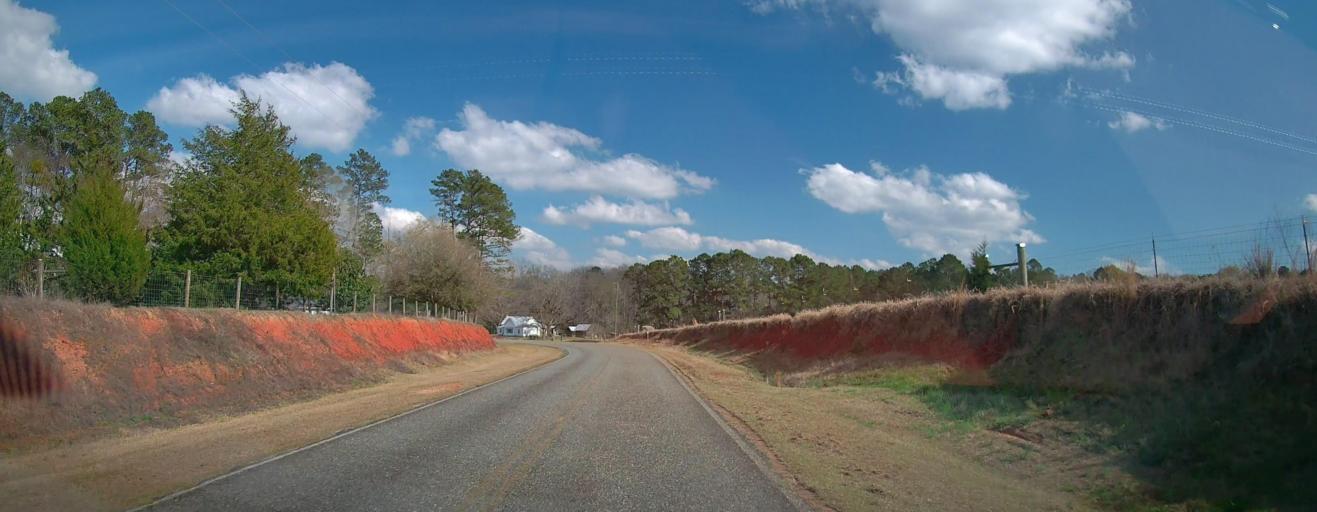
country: US
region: Georgia
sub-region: Wilkinson County
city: Irwinton
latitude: 32.6409
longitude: -83.1787
